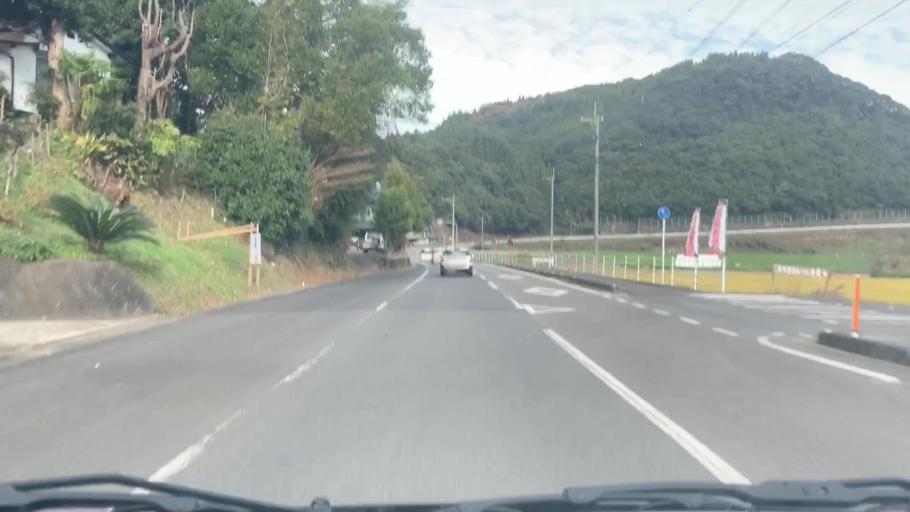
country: JP
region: Saga Prefecture
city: Imaricho-ko
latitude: 33.3253
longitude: 129.9689
